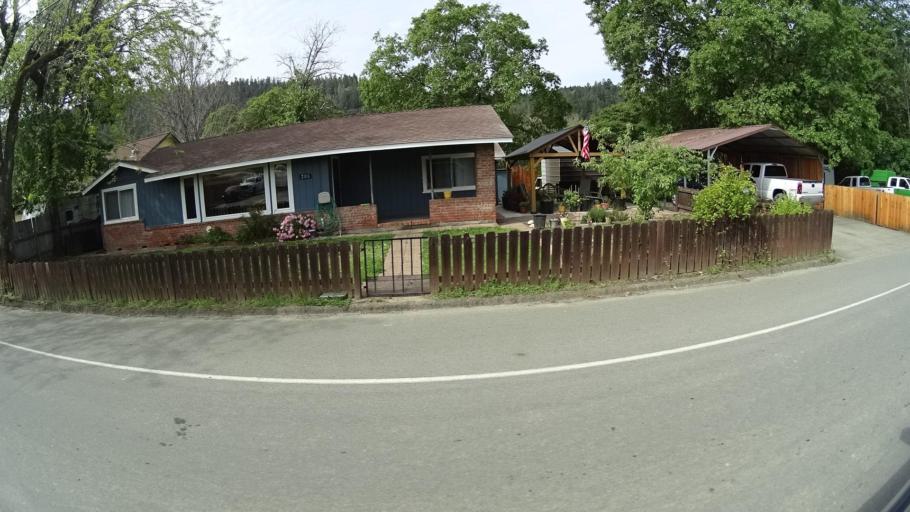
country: US
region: California
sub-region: Humboldt County
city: Redway
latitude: 40.1185
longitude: -123.8289
